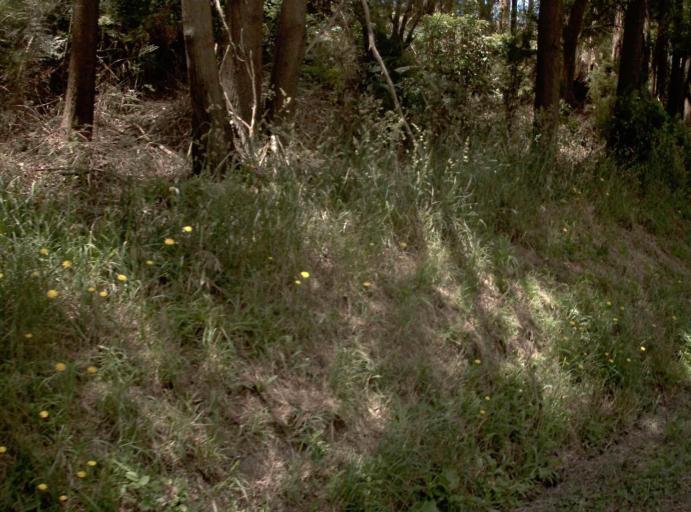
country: AU
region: Victoria
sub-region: Bass Coast
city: North Wonthaggi
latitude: -38.7223
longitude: 146.1208
